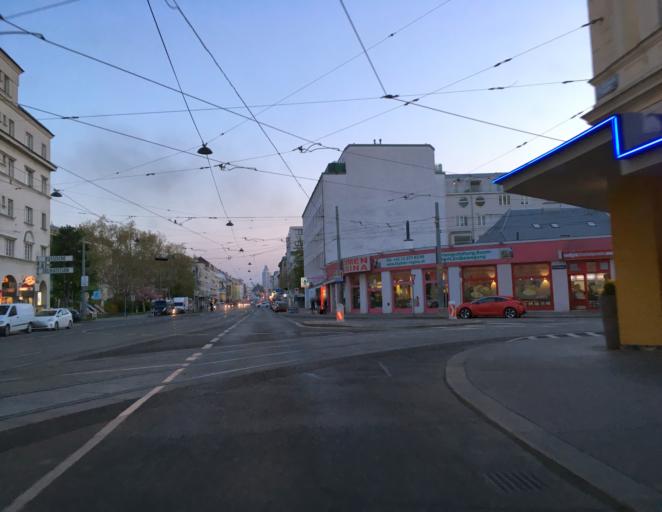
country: AT
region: Vienna
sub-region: Wien Stadt
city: Vienna
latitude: 48.2624
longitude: 16.4004
